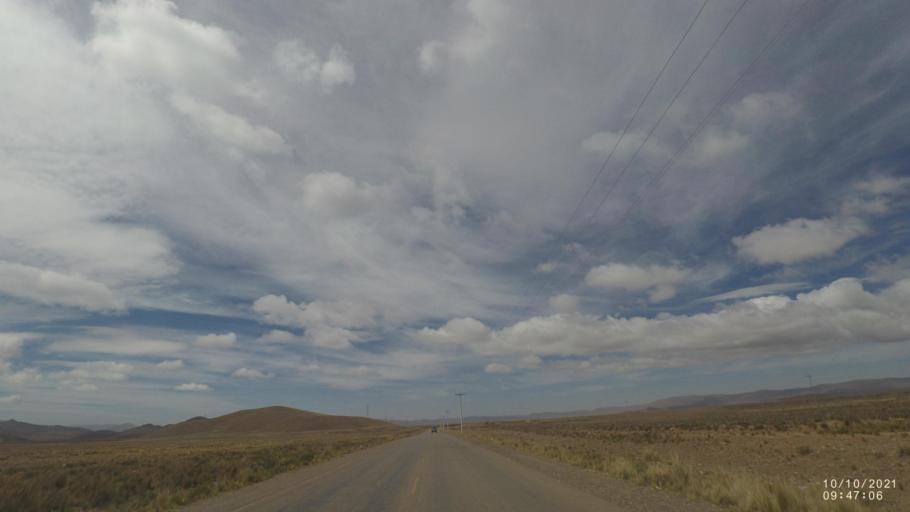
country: BO
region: La Paz
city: Quime
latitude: -17.1891
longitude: -67.3406
